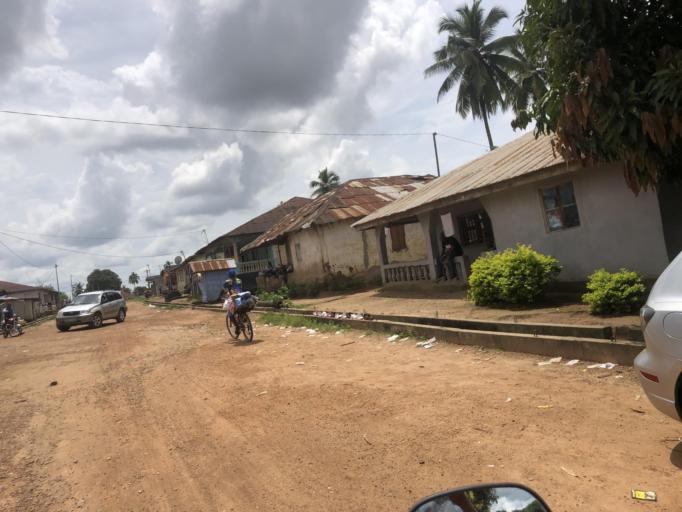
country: SL
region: Northern Province
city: Makeni
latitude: 8.8797
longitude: -12.0510
